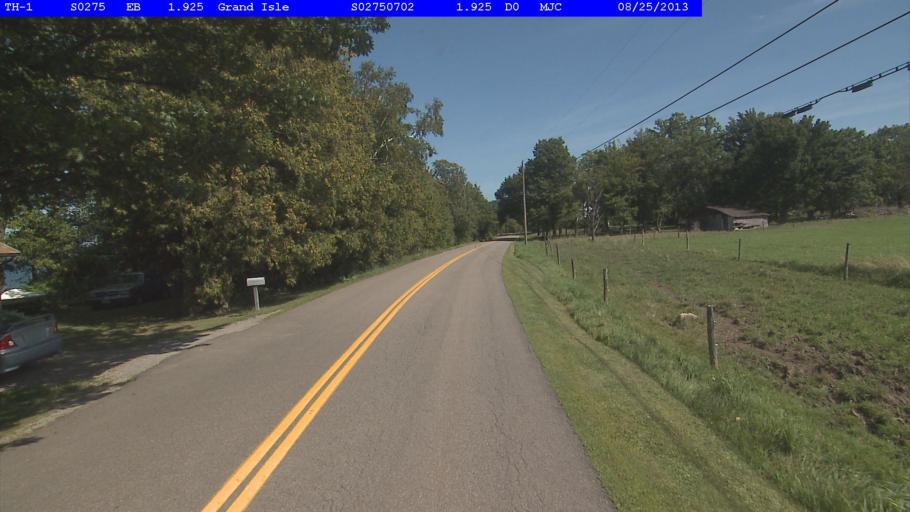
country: US
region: New York
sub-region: Clinton County
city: Cumberland Head
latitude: 44.7275
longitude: -73.3376
